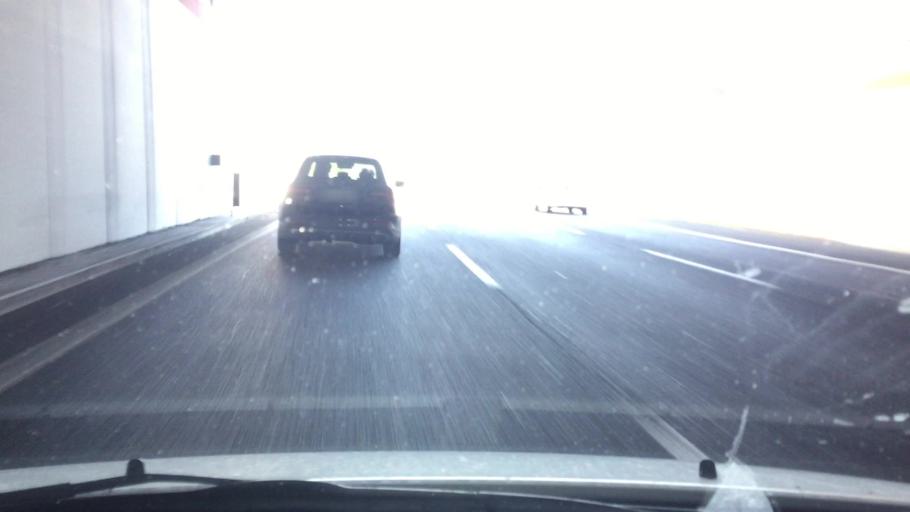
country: VA
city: Vatican City
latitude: 41.9681
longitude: 12.4030
